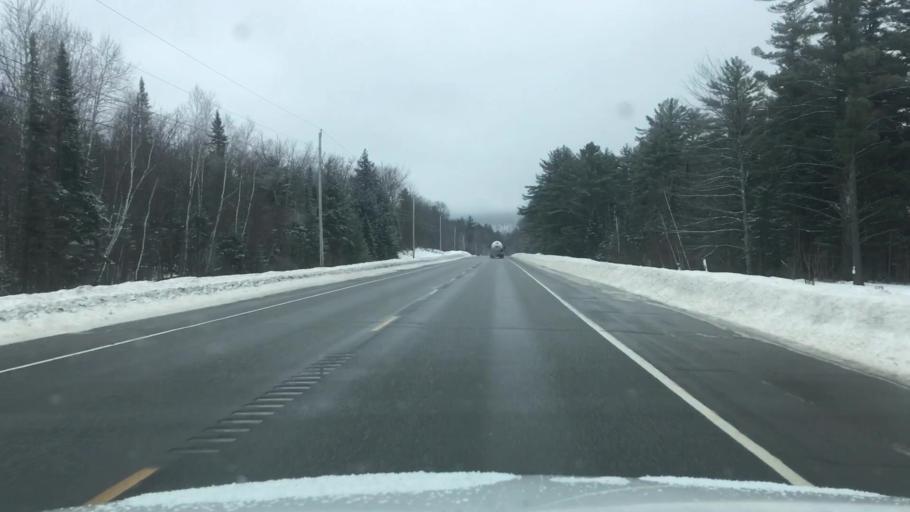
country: US
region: Maine
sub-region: Oxford County
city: Peru
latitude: 44.5813
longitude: -70.3353
